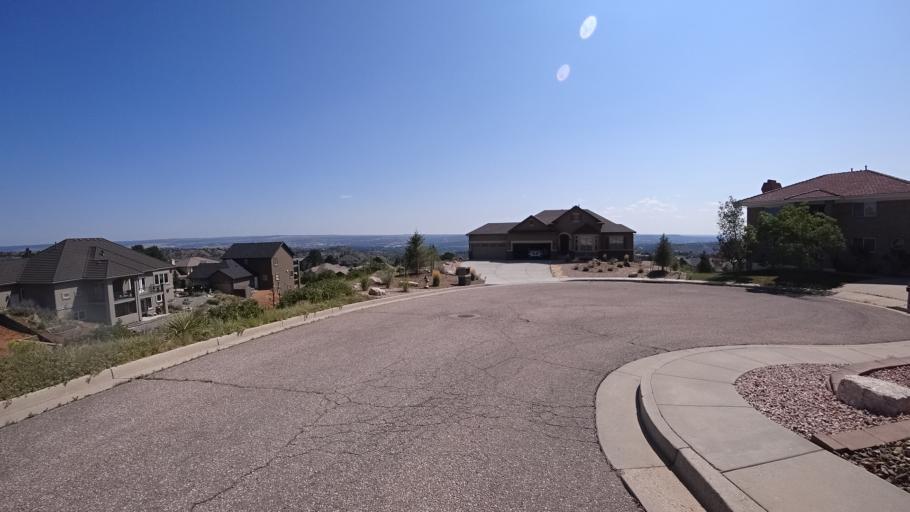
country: US
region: Colorado
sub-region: El Paso County
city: Manitou Springs
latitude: 38.9208
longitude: -104.8774
